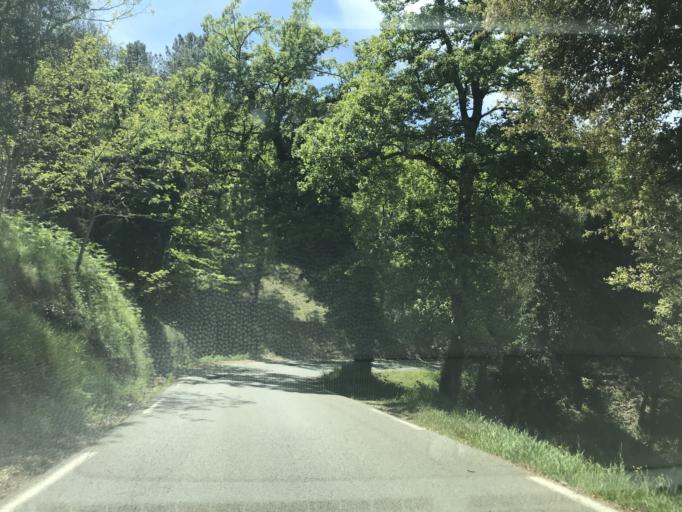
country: FR
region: Provence-Alpes-Cote d'Azur
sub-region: Departement du Var
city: Tanneron
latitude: 43.5852
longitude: 6.8217
